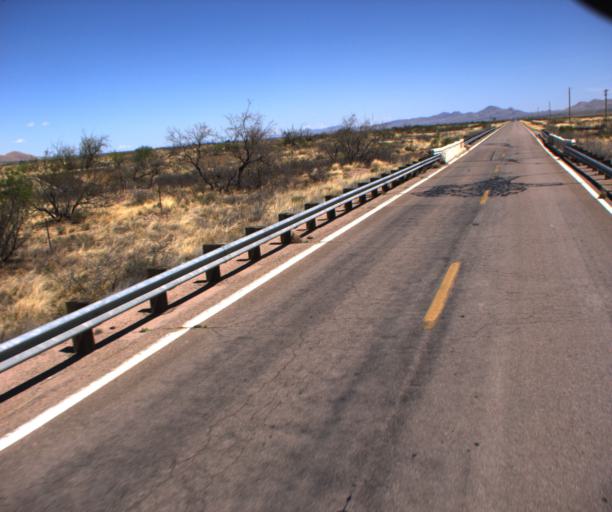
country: US
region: Arizona
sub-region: Cochise County
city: Douglas
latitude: 31.7667
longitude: -109.0799
